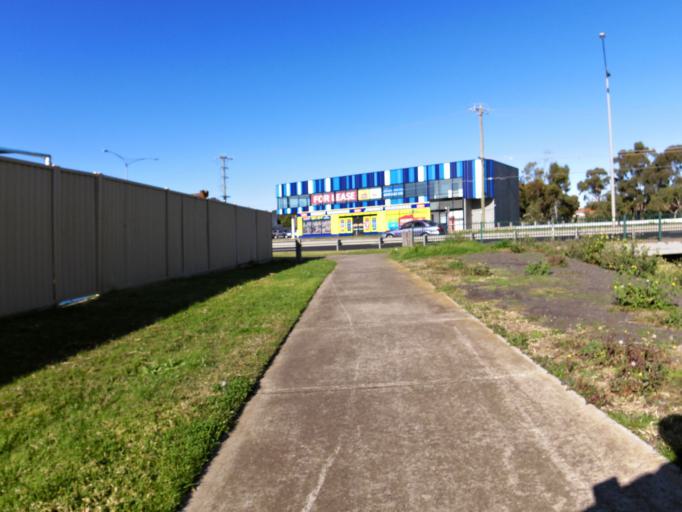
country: AU
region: Victoria
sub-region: Wyndham
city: Tarneit
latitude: -37.8764
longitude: 144.6752
